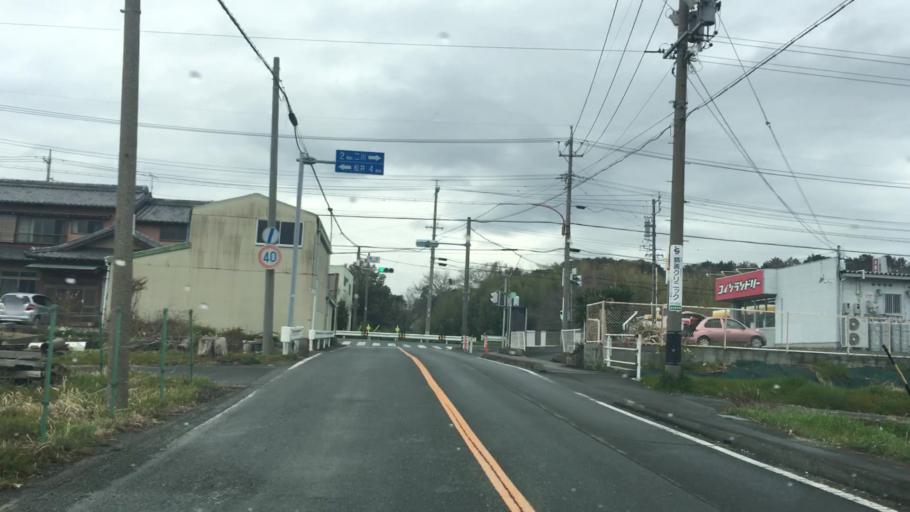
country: JP
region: Aichi
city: Toyohashi
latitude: 34.7230
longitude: 137.4177
